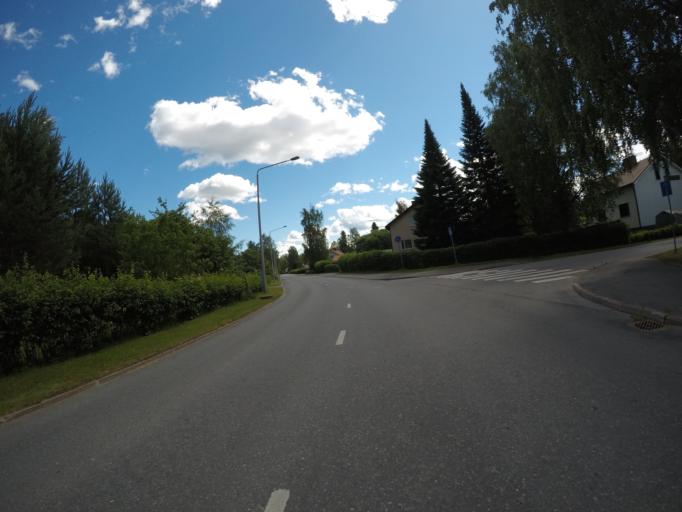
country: FI
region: Haeme
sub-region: Haemeenlinna
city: Haemeenlinna
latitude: 61.0127
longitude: 24.4301
